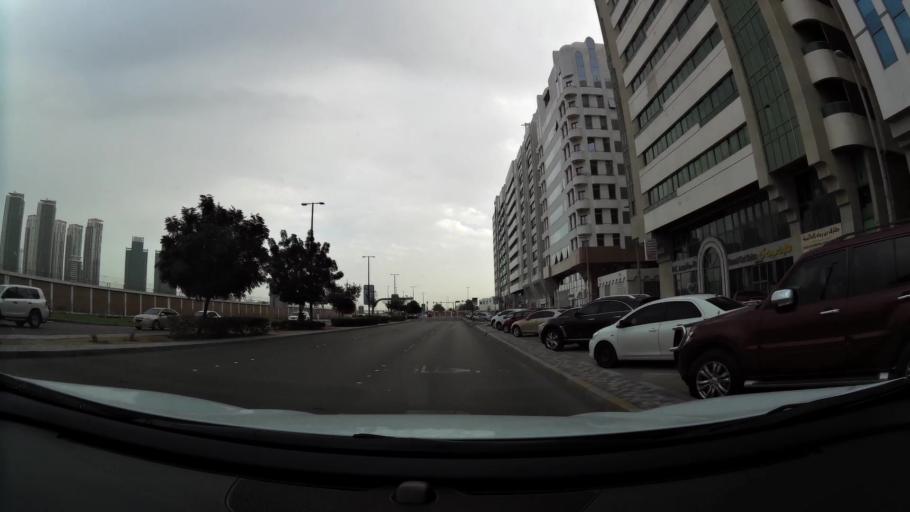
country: AE
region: Abu Dhabi
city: Abu Dhabi
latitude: 24.4914
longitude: 54.3841
